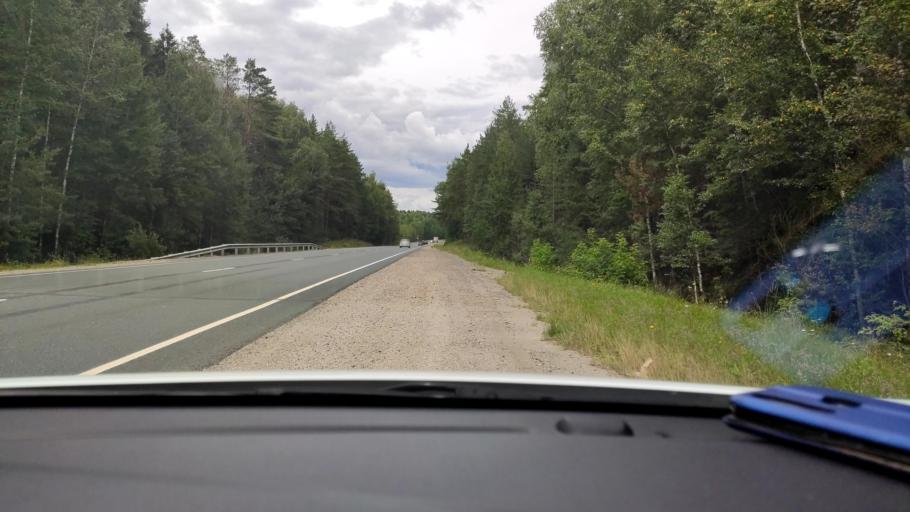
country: RU
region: Mariy-El
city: Pomary
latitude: 56.0029
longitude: 48.3815
